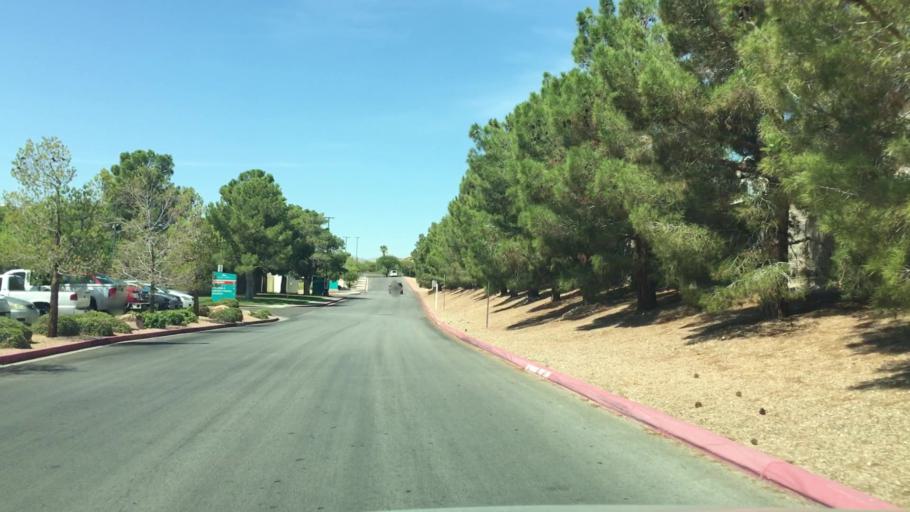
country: US
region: Nevada
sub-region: Clark County
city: Summerlin South
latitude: 36.1828
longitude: -115.3178
